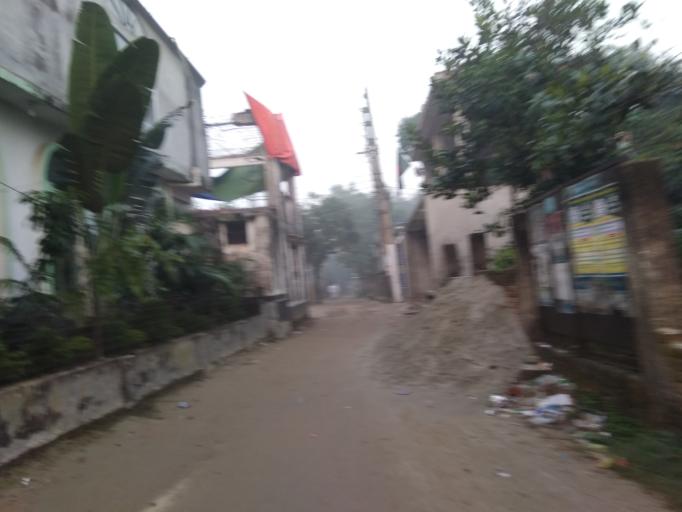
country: BD
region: Dhaka
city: Tungi
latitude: 23.8571
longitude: 90.4350
